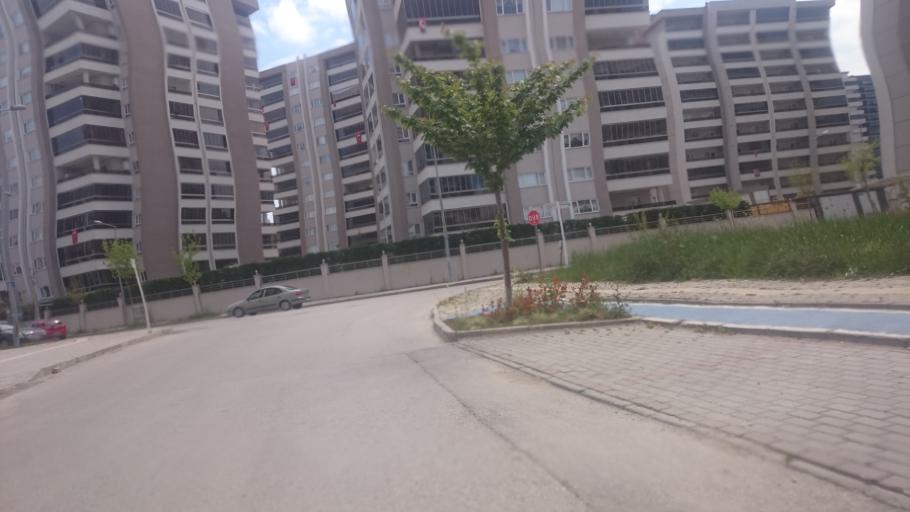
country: TR
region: Bursa
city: Cali
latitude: 40.2198
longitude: 28.9416
